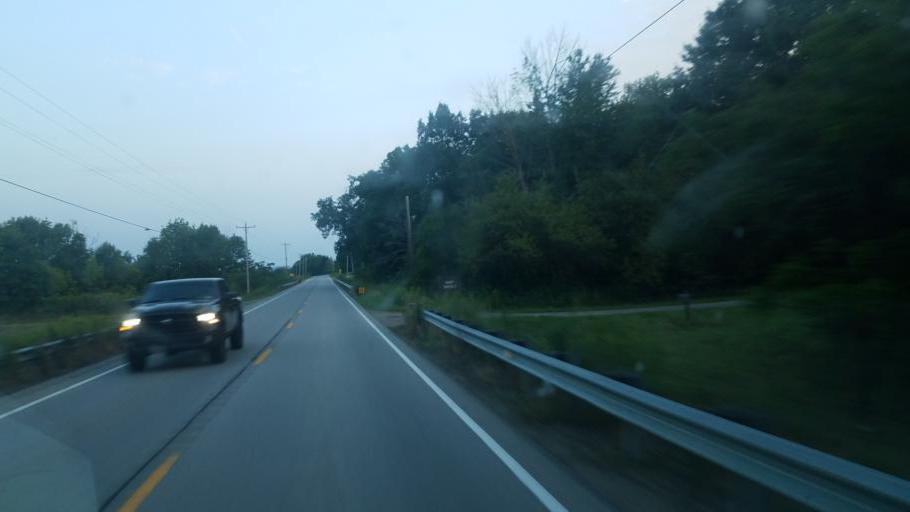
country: US
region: Pennsylvania
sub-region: Crawford County
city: Meadville
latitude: 41.5535
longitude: -80.2060
